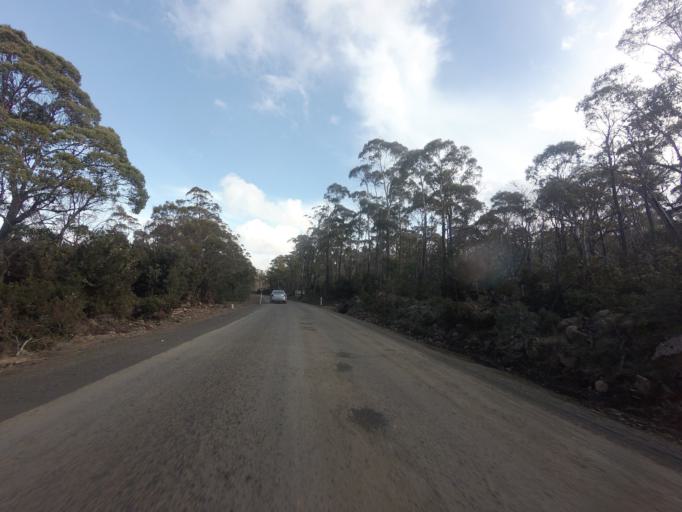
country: AU
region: Tasmania
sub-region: Meander Valley
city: Deloraine
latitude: -41.7802
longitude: 146.7074
